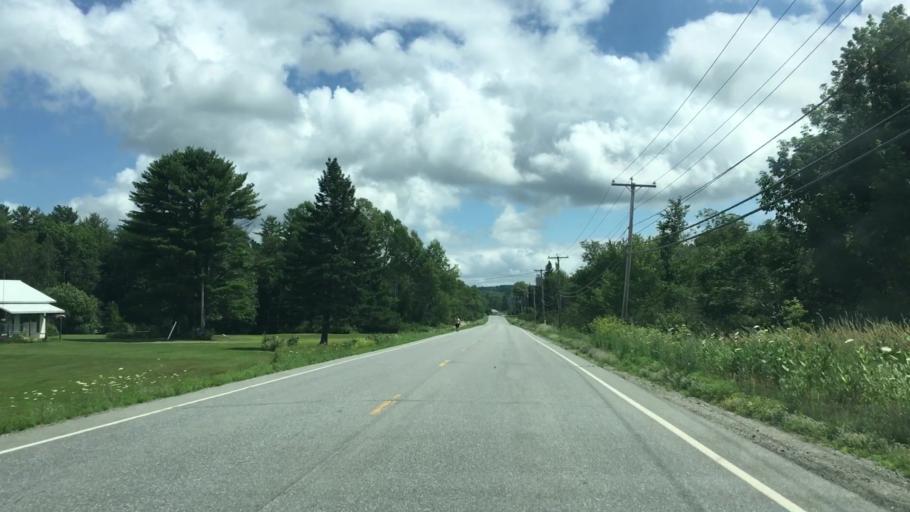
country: US
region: Maine
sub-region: Penobscot County
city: Carmel
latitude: 44.8080
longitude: -68.9870
